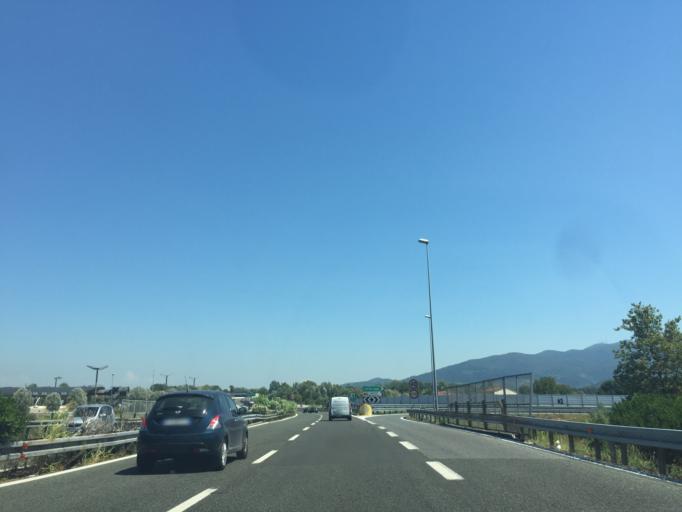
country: IT
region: Tuscany
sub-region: Provincia di Lucca
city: Lucca
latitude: 43.8380
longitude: 10.4647
